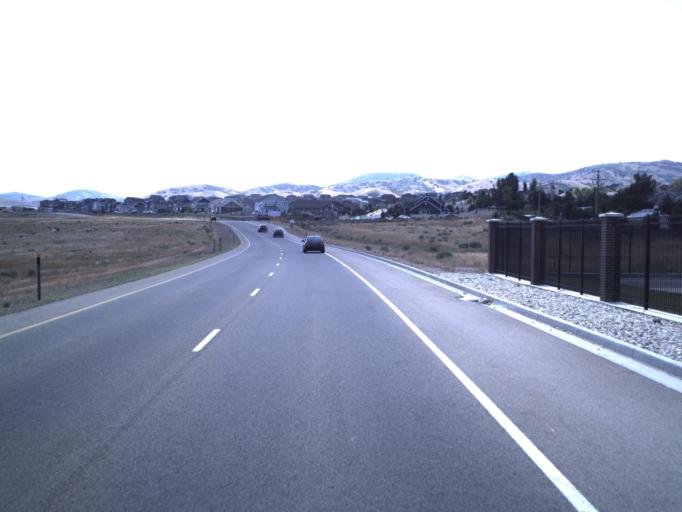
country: US
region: Utah
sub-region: Salt Lake County
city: Herriman
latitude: 40.4961
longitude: -112.0050
